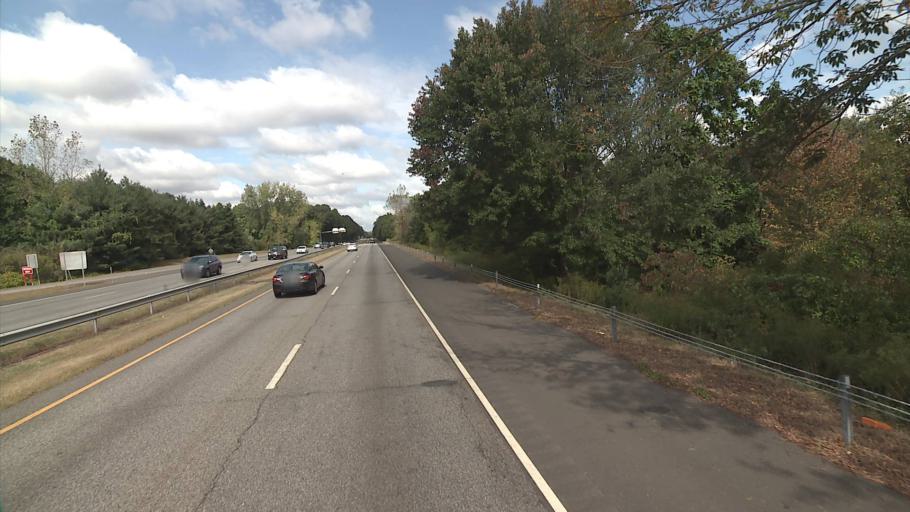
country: US
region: Connecticut
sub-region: New Haven County
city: Wallingford
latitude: 41.4658
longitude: -72.8313
